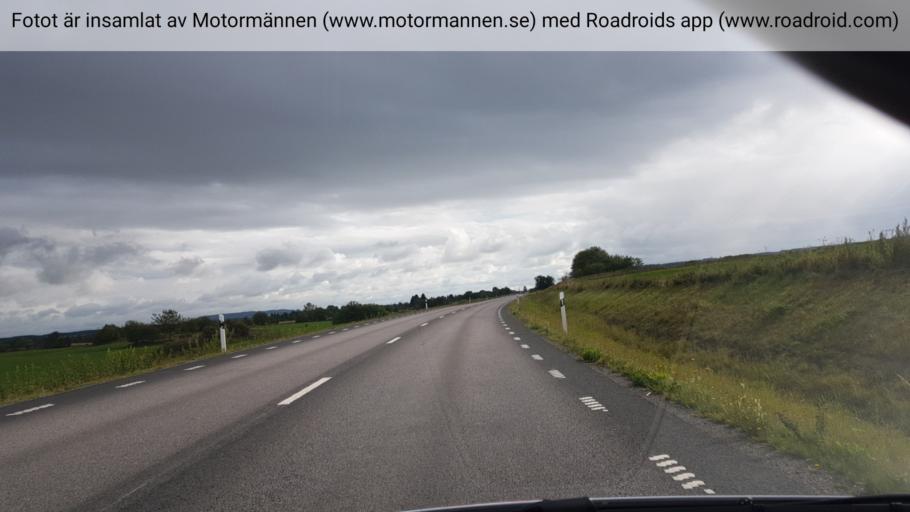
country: SE
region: Vaestra Goetaland
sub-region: Falkopings Kommun
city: Falkoeping
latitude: 58.2219
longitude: 13.5655
